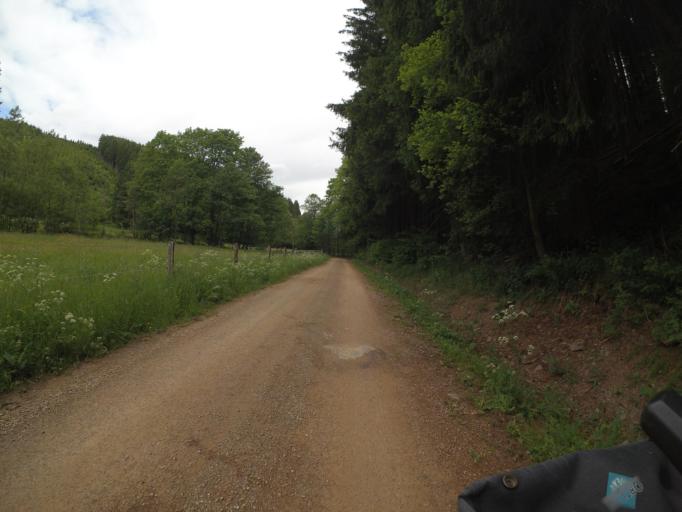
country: DE
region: North Rhine-Westphalia
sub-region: Regierungsbezirk Koln
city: Hellenthal
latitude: 50.4380
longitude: 6.4079
